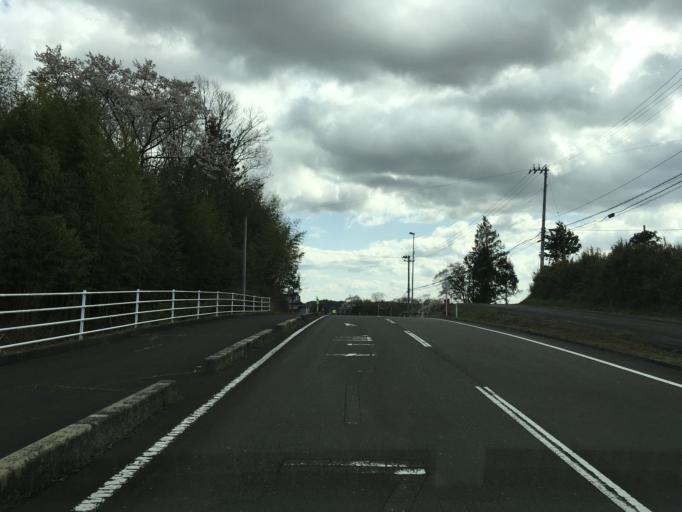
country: JP
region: Iwate
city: Ichinoseki
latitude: 38.7510
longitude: 141.2667
